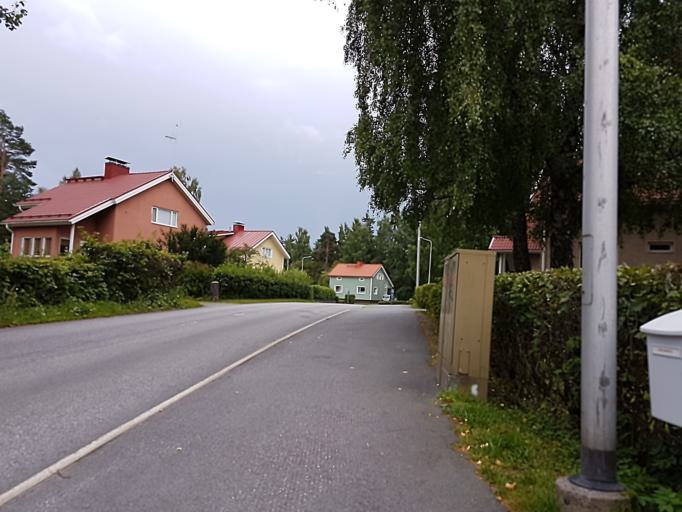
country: FI
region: Pirkanmaa
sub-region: Etelae-Pirkanmaa
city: Valkeakoski
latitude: 61.2600
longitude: 24.0426
